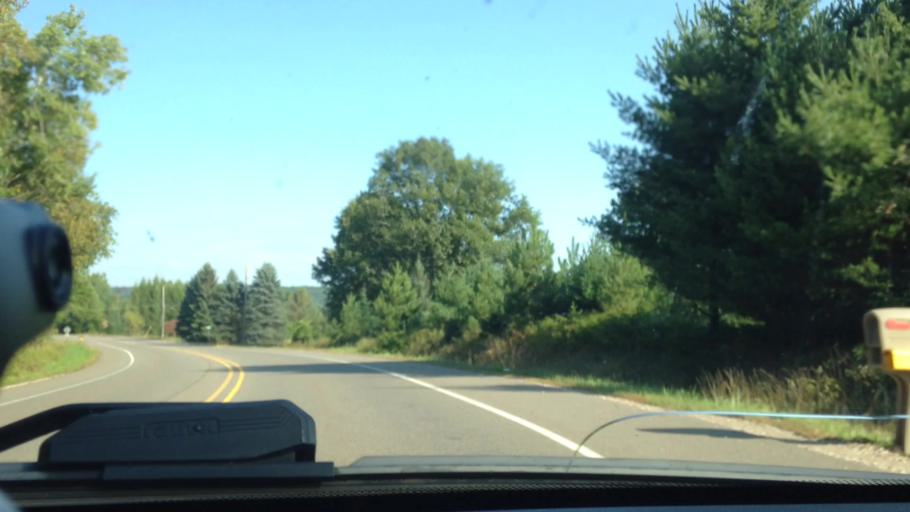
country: US
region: Michigan
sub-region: Dickinson County
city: Quinnesec
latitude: 45.8262
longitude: -87.9921
